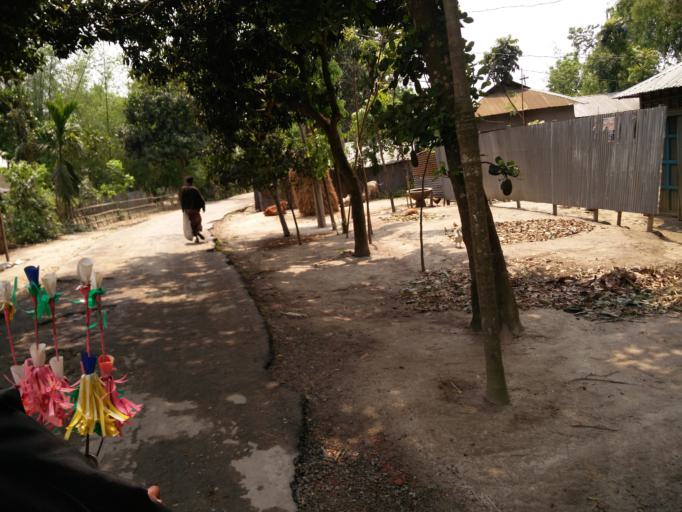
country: BD
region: Dhaka
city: Sherpur
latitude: 24.9394
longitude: 90.1600
